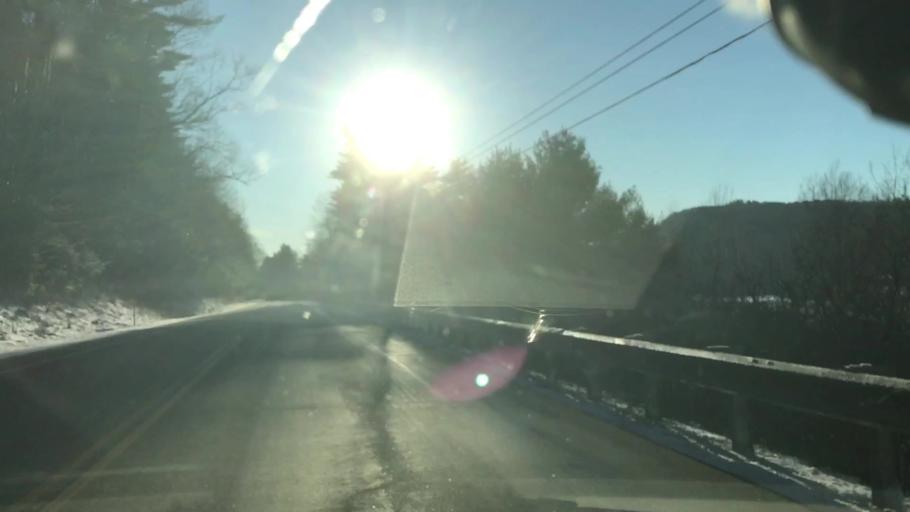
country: US
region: New Hampshire
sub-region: Grafton County
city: Orford
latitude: 43.9526
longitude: -72.1000
